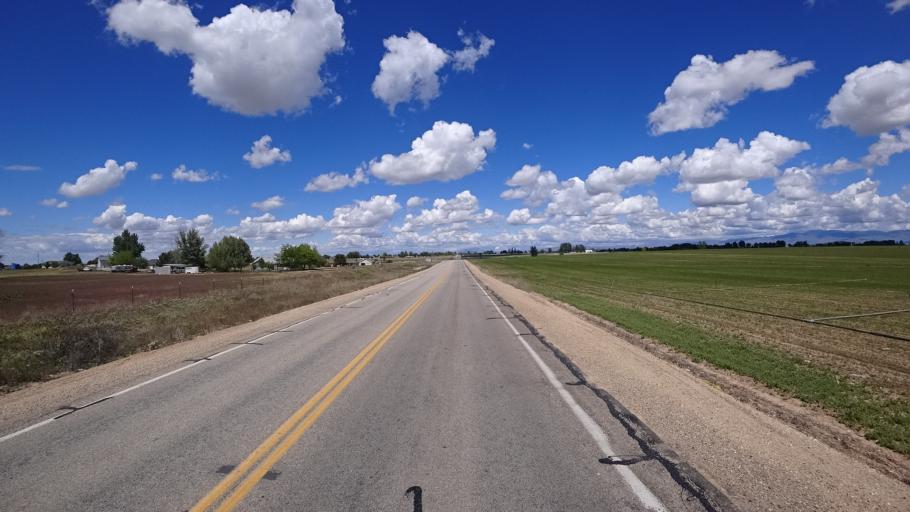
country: US
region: Idaho
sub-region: Ada County
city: Meridian
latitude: 43.5653
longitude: -116.4341
